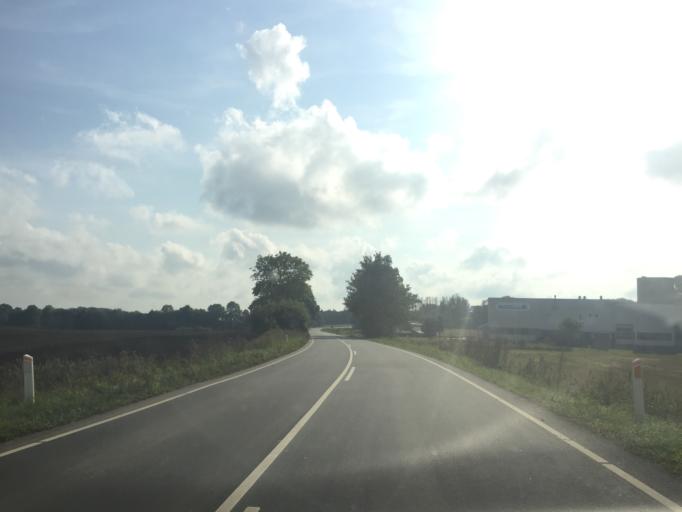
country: DK
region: Zealand
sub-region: Holbaek Kommune
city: Tollose
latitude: 55.6305
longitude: 11.7886
